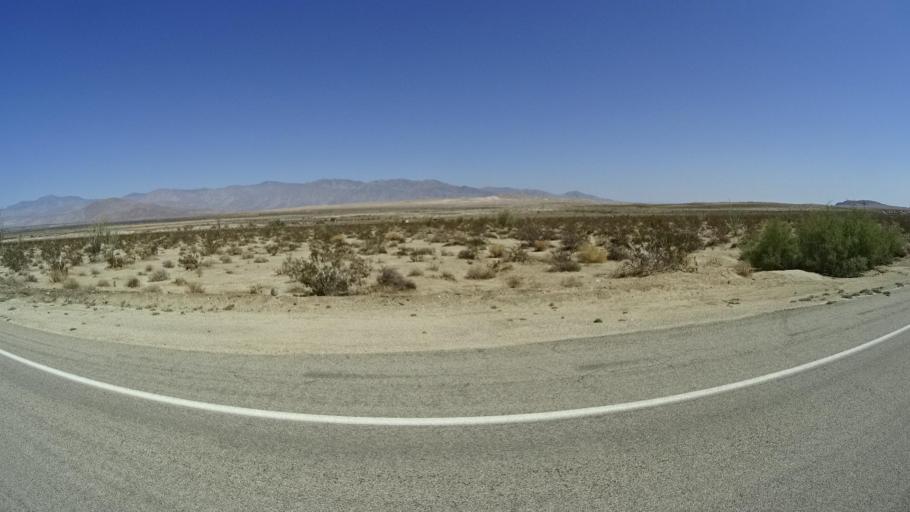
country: US
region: California
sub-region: San Diego County
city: Borrego Springs
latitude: 33.1965
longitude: -116.3064
